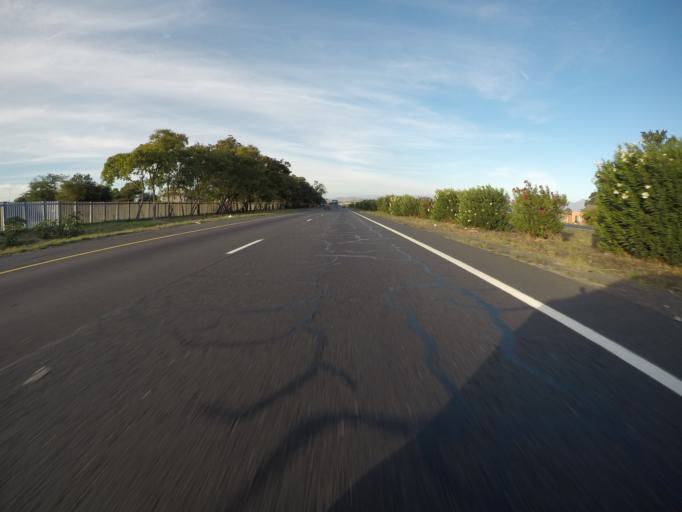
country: ZA
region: Western Cape
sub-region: City of Cape Town
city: Kraaifontein
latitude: -33.8508
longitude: 18.7065
